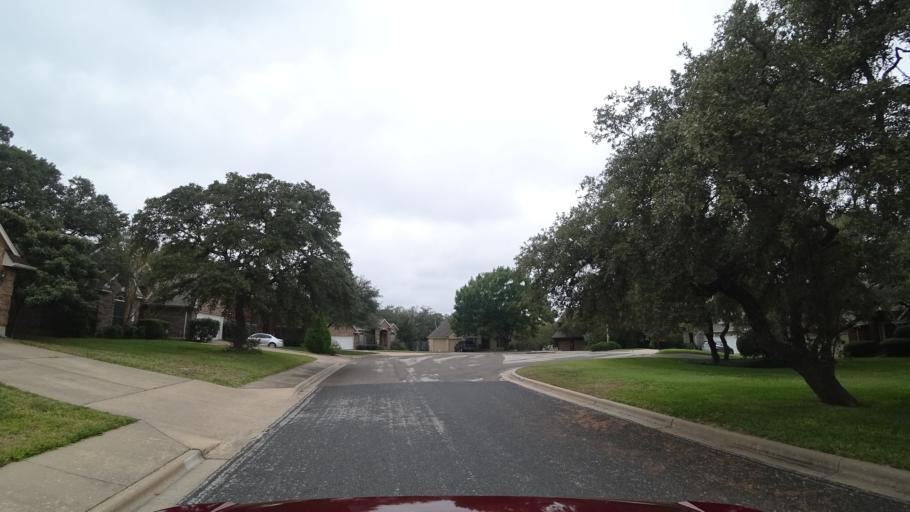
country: US
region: Texas
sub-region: Williamson County
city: Anderson Mill
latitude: 30.4375
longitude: -97.8215
